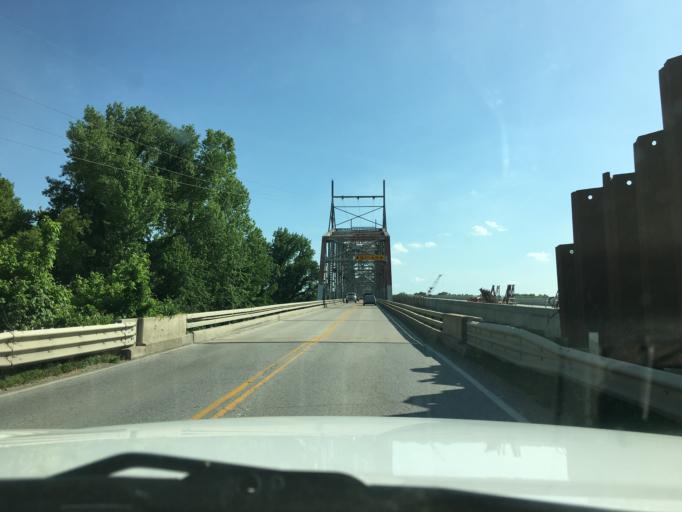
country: US
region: Missouri
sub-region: Franklin County
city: Washington
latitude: 38.5613
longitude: -90.9956
